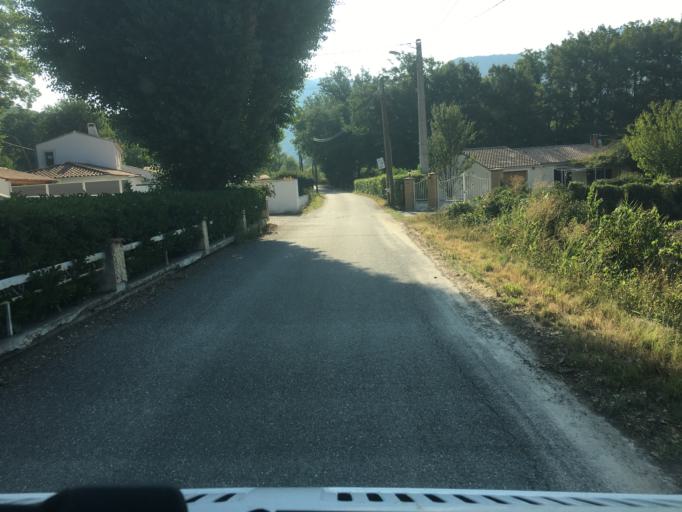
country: FR
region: Provence-Alpes-Cote d'Azur
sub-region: Departement des Alpes-de-Haute-Provence
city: Mallemoisson
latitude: 43.9411
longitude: 6.1791
